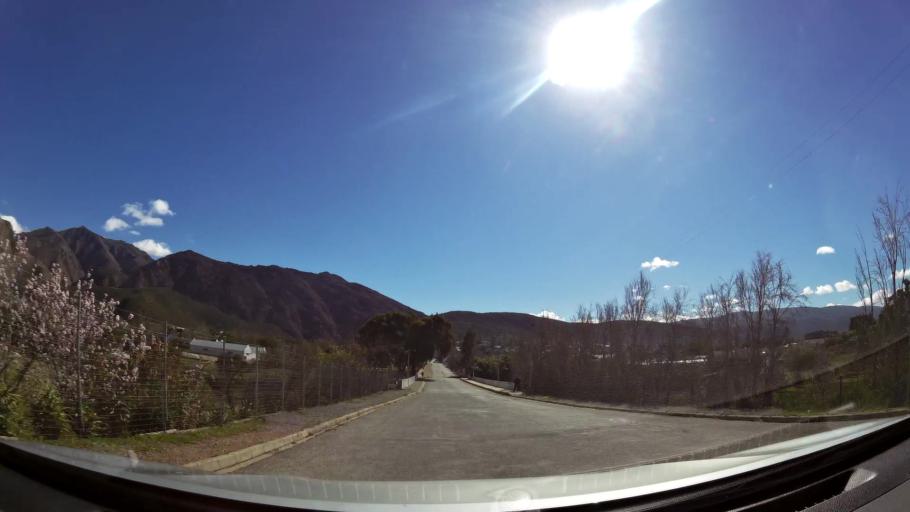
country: ZA
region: Western Cape
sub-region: Cape Winelands District Municipality
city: Ashton
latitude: -33.7927
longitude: 20.1205
